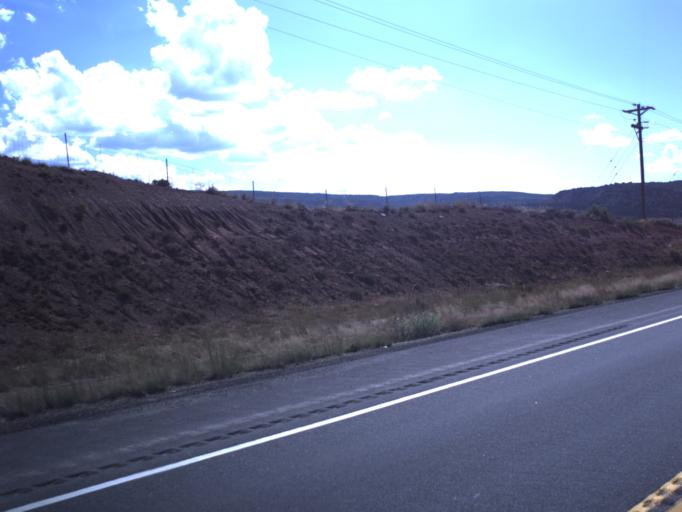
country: US
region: Utah
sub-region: Duchesne County
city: Duchesne
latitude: 40.2124
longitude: -110.8577
